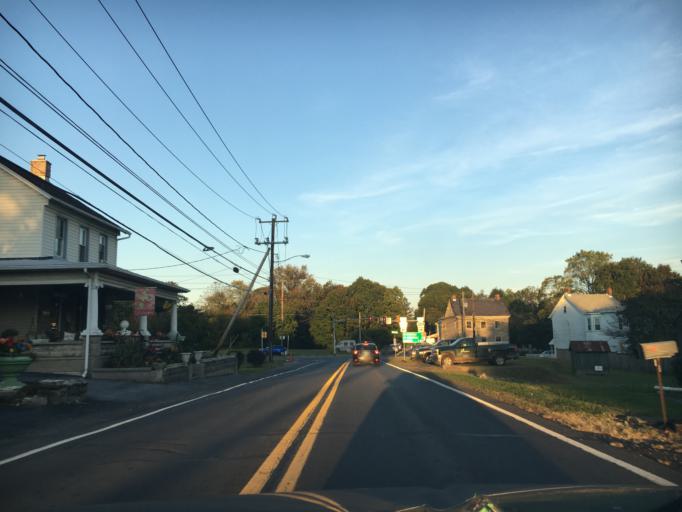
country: US
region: Pennsylvania
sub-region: Lehigh County
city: Schnecksville
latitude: 40.6349
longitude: -75.5859
